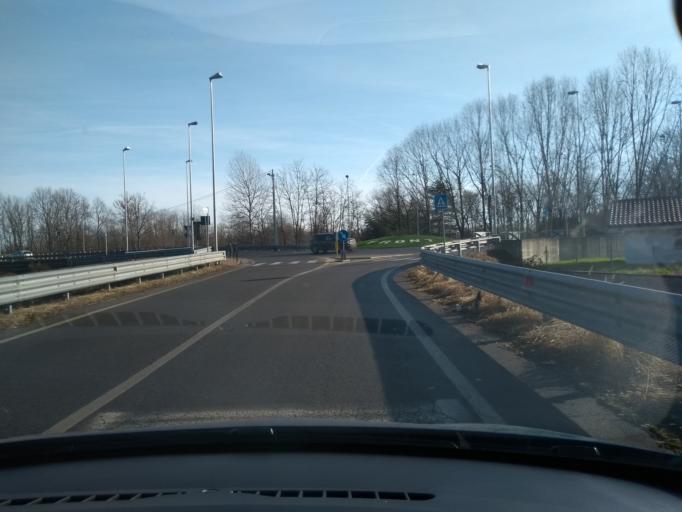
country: IT
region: Piedmont
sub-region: Provincia di Torino
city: Front
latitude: 45.2828
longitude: 7.6644
